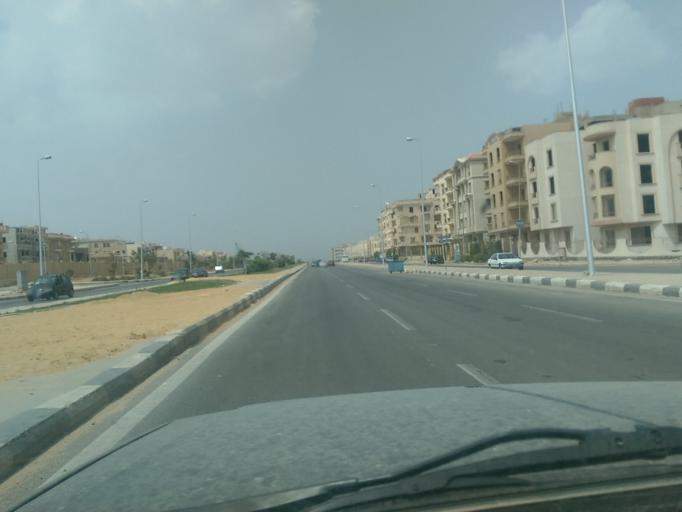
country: EG
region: Muhafazat al Qahirah
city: Cairo
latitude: 29.9959
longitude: 31.4396
